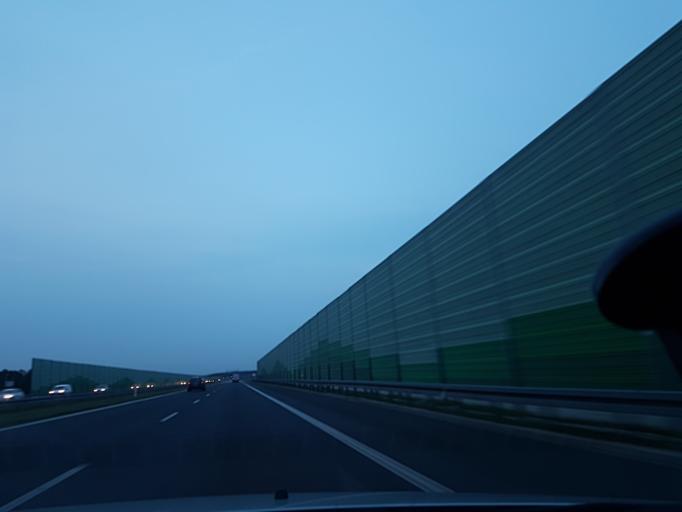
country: PL
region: Lodz Voivodeship
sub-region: Powiat leczycki
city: Piatek
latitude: 52.0893
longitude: 19.5217
